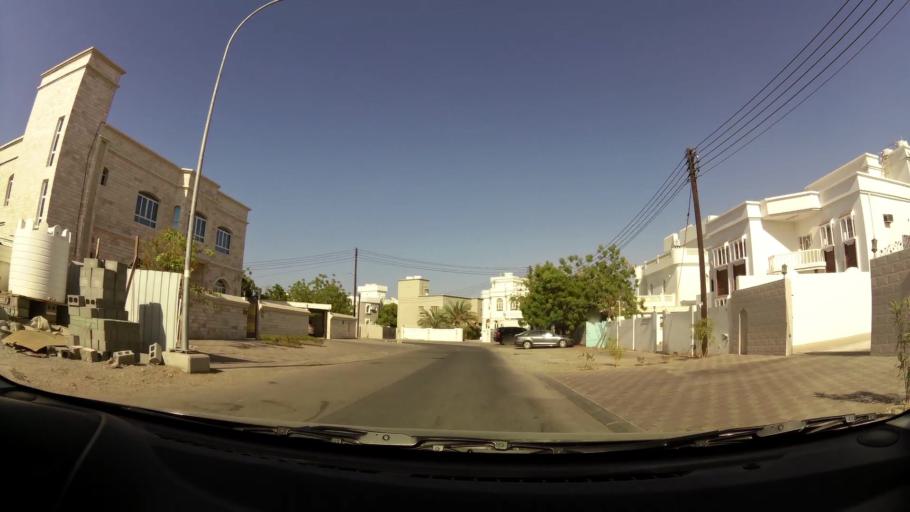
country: OM
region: Muhafazat Masqat
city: As Sib al Jadidah
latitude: 23.6157
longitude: 58.2120
